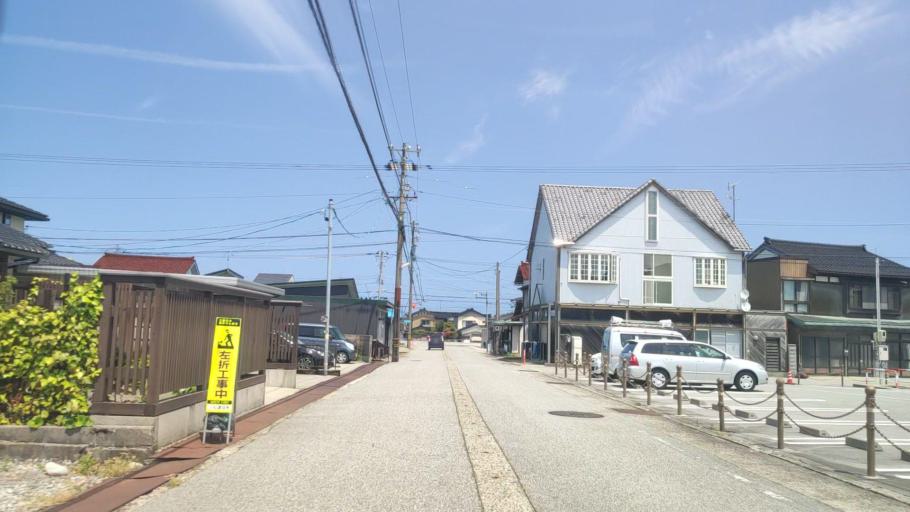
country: JP
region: Toyama
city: Nyuzen
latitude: 36.9575
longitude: 137.5592
